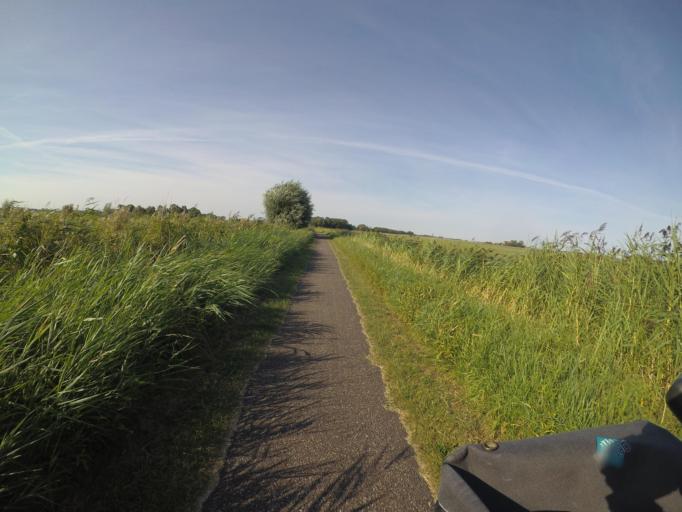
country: NL
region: Friesland
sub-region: Gemeente Dantumadiel
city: Rinsumageast
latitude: 53.3210
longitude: 5.9531
